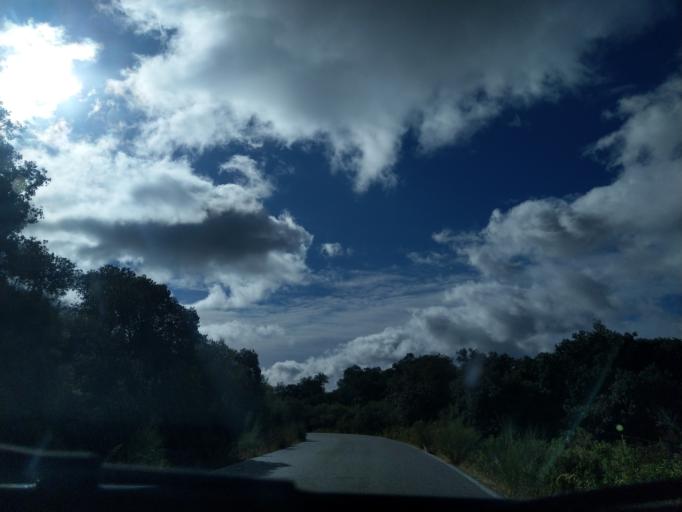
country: ES
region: Extremadura
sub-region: Provincia de Badajoz
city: Reina
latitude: 38.1389
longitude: -5.9164
